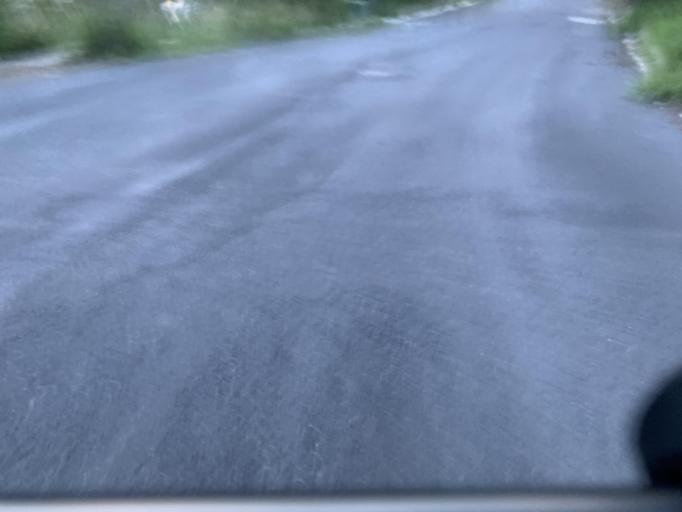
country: MX
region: Nuevo Leon
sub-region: Juarez
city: Bosques de San Pedro
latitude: 25.5184
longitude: -100.1850
